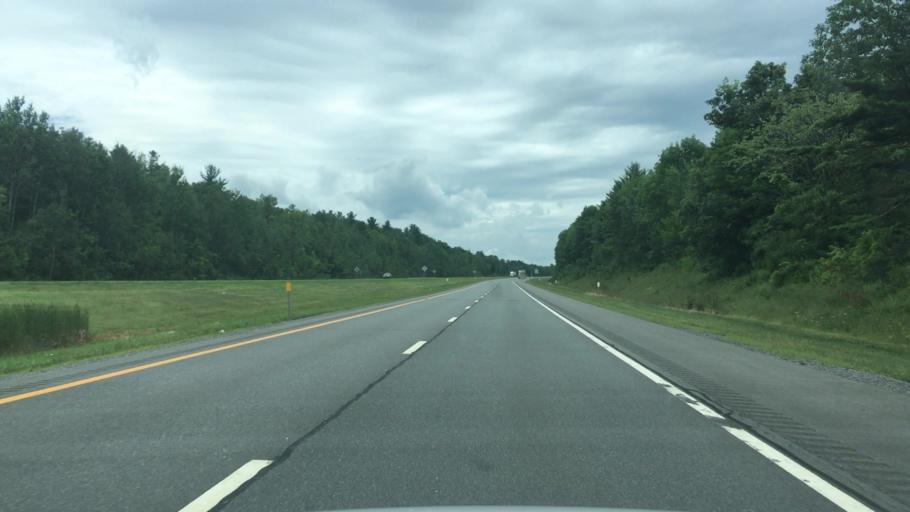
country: US
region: New York
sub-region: Schoharie County
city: Schoharie
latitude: 42.7203
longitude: -74.2506
